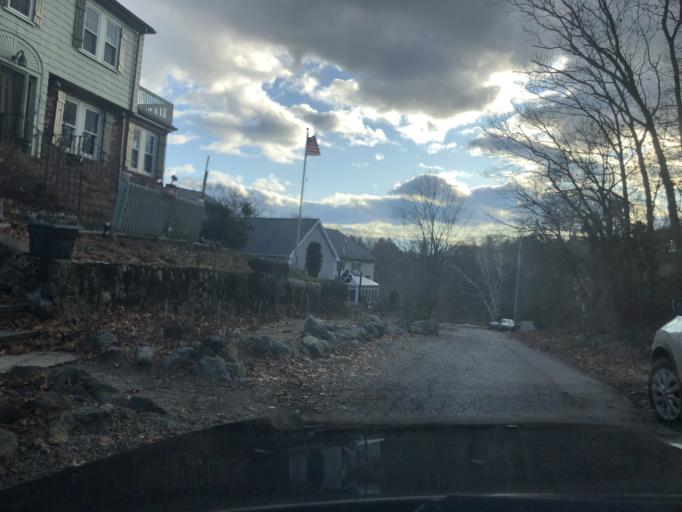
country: US
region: Massachusetts
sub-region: Middlesex County
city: Arlington
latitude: 42.4129
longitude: -71.1657
